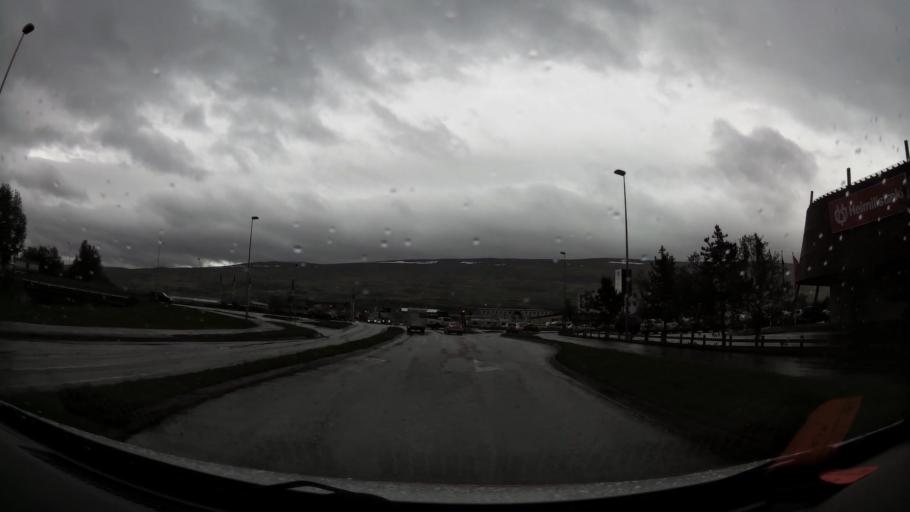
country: IS
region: Northeast
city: Akureyri
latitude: 65.6882
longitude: -18.1028
